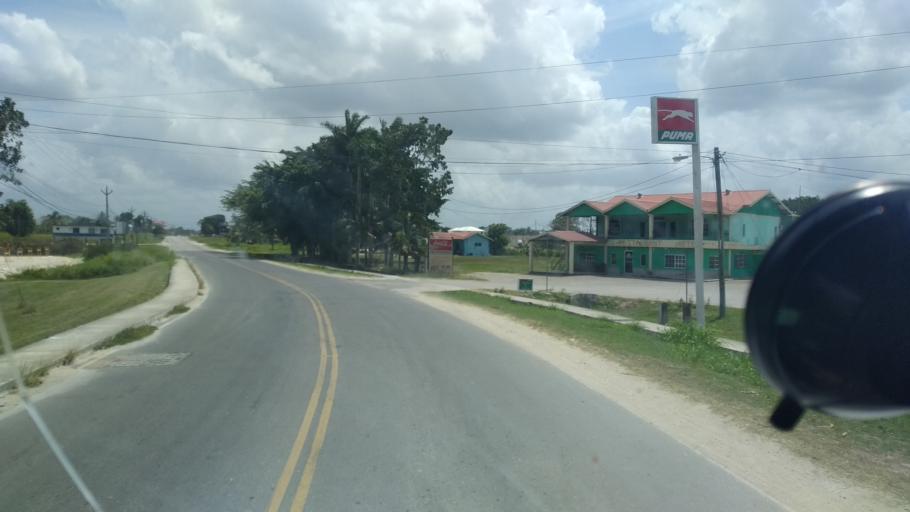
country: BZ
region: Orange Walk
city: Orange Walk
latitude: 18.0621
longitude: -88.5723
